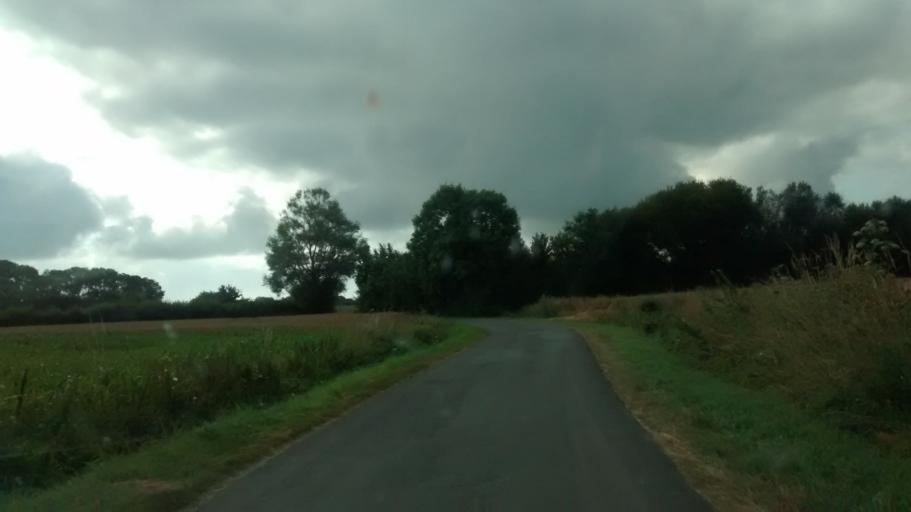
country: FR
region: Brittany
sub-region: Departement d'Ille-et-Vilaine
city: La Gouesniere
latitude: 48.6049
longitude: -1.8763
